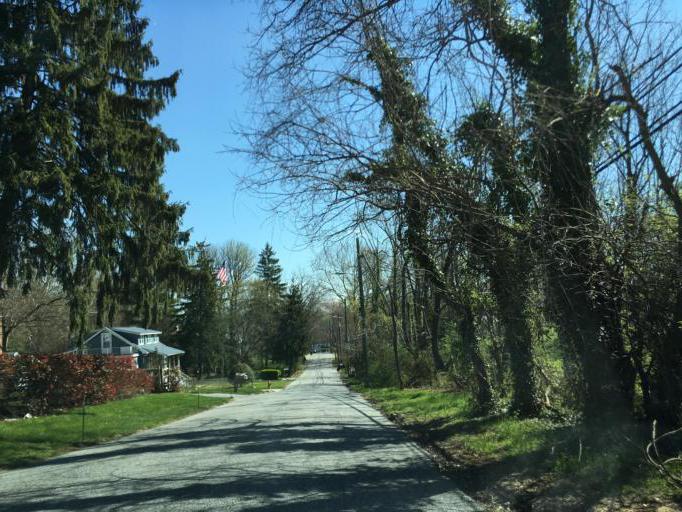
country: US
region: Maryland
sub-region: Baltimore County
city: Lutherville
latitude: 39.4183
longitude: -76.6121
